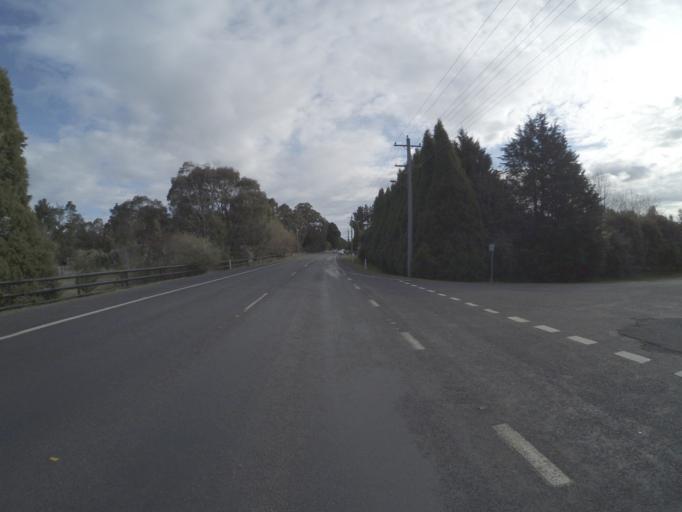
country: AU
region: New South Wales
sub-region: Wingecarribee
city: Moss Vale
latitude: -34.5747
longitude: 150.3120
